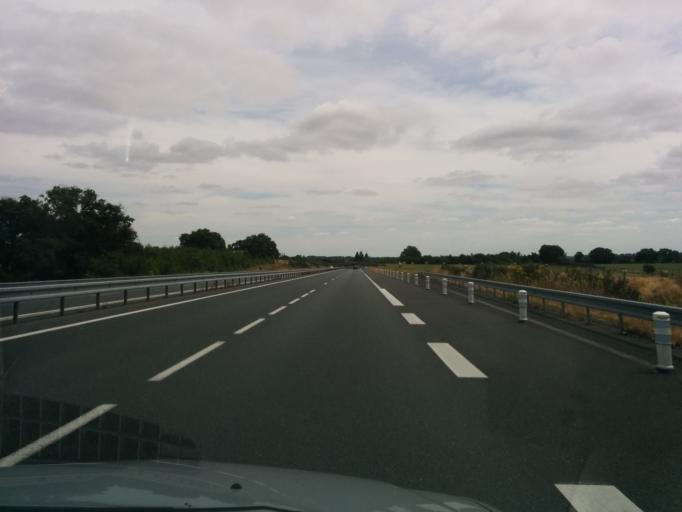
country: FR
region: Pays de la Loire
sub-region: Departement de Maine-et-Loire
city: La Tessoualle
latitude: 46.9728
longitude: -0.8091
